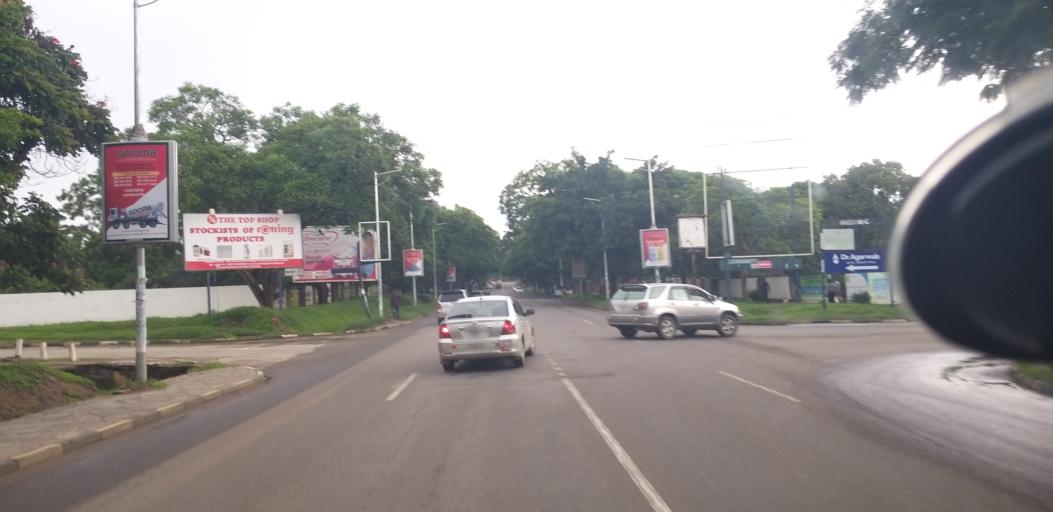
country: ZM
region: Lusaka
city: Lusaka
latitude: -15.4150
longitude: 28.2899
